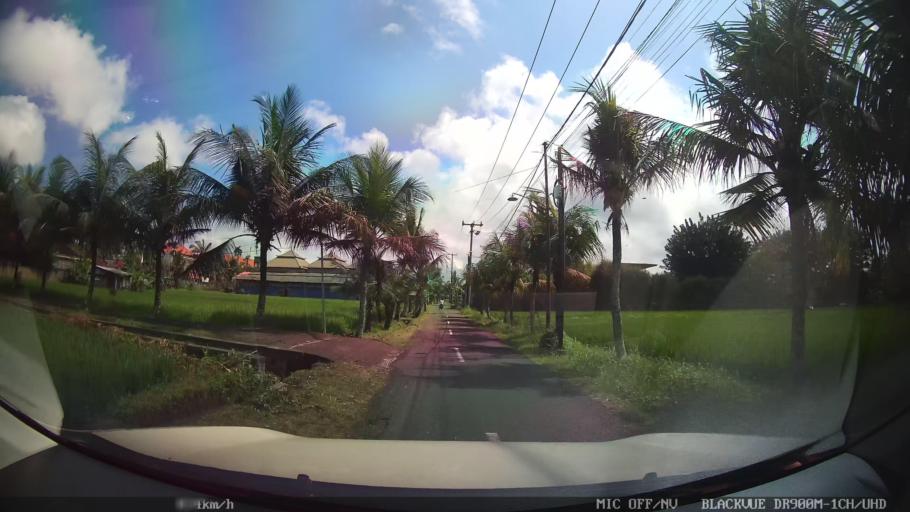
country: ID
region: Bali
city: Banjar Sedang
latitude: -8.5540
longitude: 115.2753
